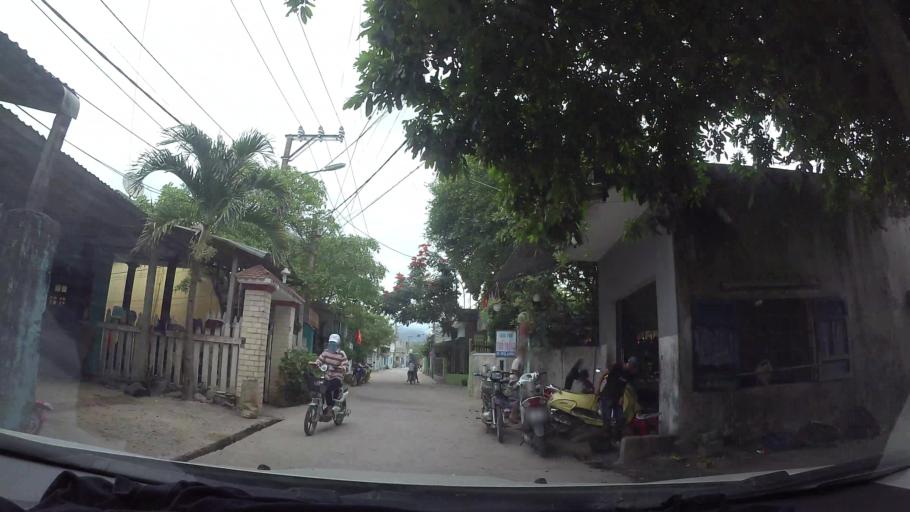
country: VN
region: Da Nang
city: Lien Chieu
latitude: 16.0870
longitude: 108.1024
